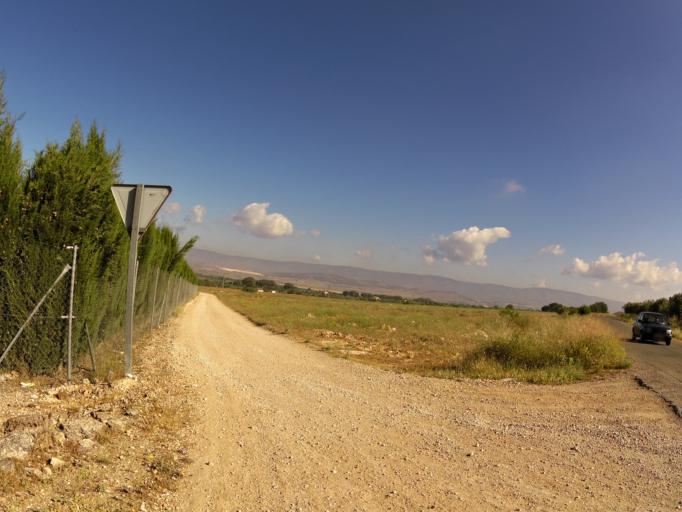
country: ES
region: Valencia
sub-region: Provincia de Alicante
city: Biar
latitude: 38.6383
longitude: -0.7677
